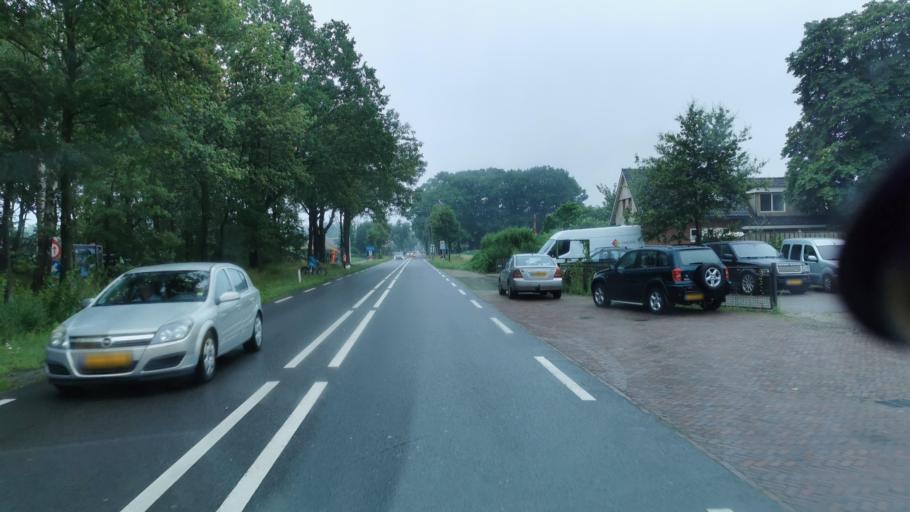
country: NL
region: Overijssel
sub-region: Gemeente Losser
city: Losser
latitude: 52.2450
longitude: 7.0290
